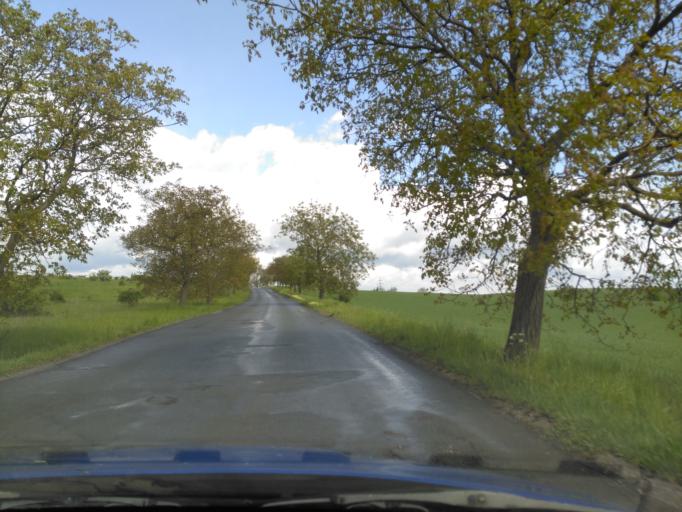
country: CZ
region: Central Bohemia
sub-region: Okres Beroun
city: Beroun
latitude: 49.9342
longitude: 14.0732
